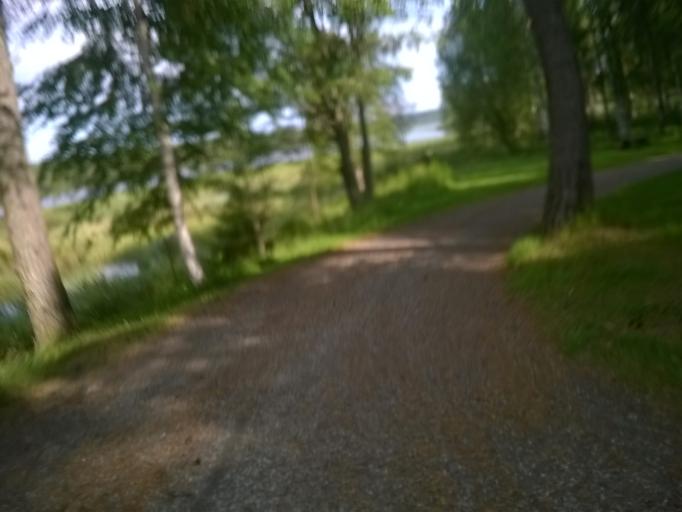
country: FI
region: Kainuu
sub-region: Kehys-Kainuu
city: Kuhmo
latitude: 64.1327
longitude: 29.5218
